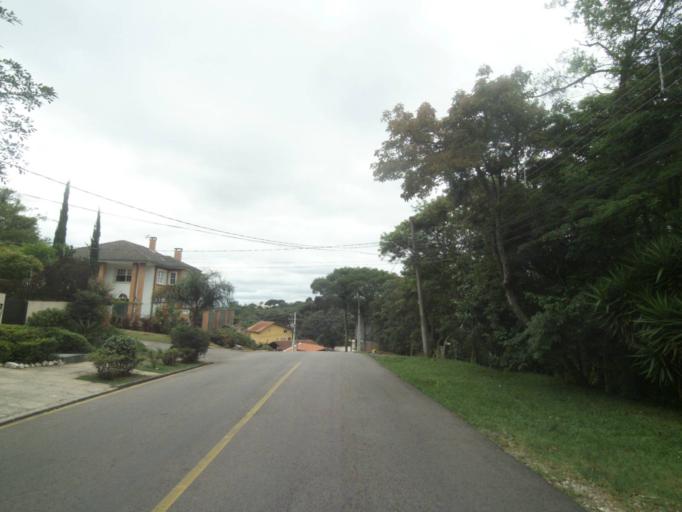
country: BR
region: Parana
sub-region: Curitiba
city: Curitiba
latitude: -25.3982
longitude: -49.2864
